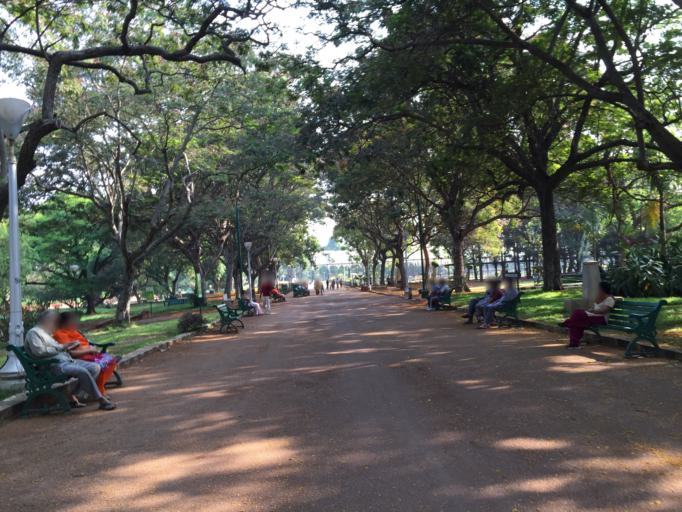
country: IN
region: Karnataka
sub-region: Bangalore Urban
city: Bangalore
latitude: 12.9483
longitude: 77.5860
